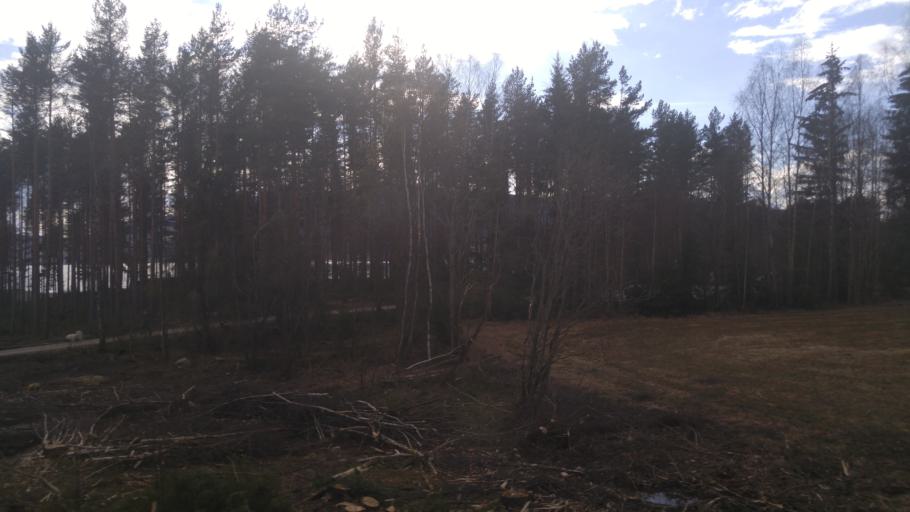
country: NO
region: Hedmark
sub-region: Ringsaker
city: Brumunddal
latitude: 60.8529
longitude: 10.9562
